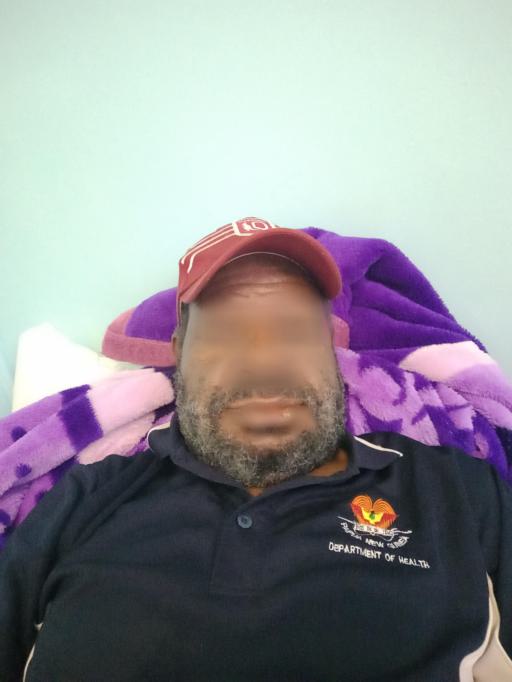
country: PG
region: Western Highlands
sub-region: Hagen
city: Mount Hagen
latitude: -5.8587
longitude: 144.2186
